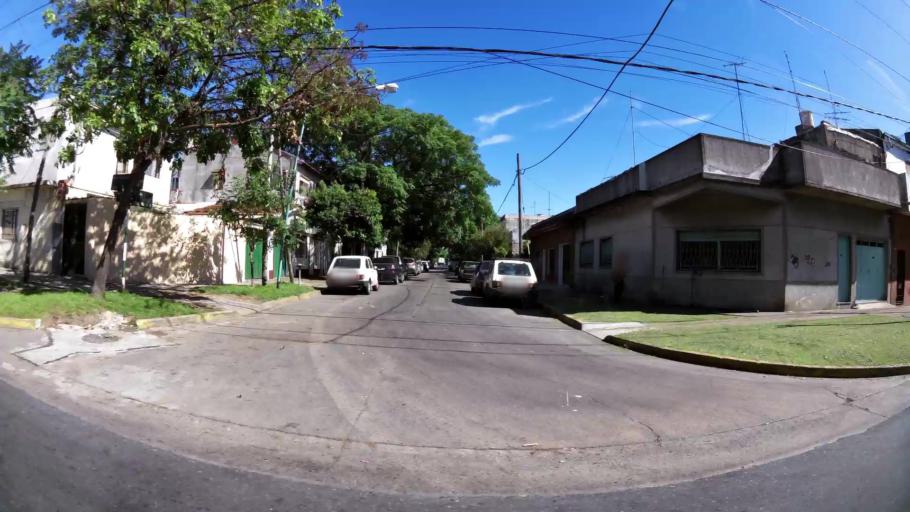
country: AR
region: Buenos Aires
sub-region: Partido de General San Martin
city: General San Martin
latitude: -34.5407
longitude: -58.5258
